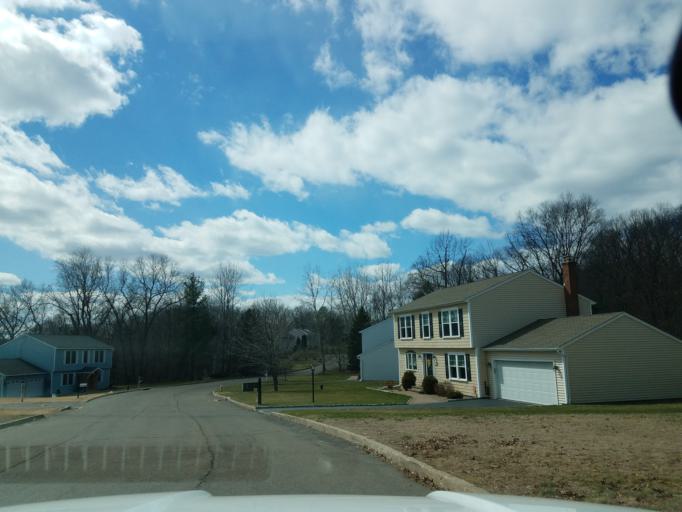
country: US
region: Connecticut
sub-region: New Haven County
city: Naugatuck
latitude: 41.4717
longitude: -73.0230
